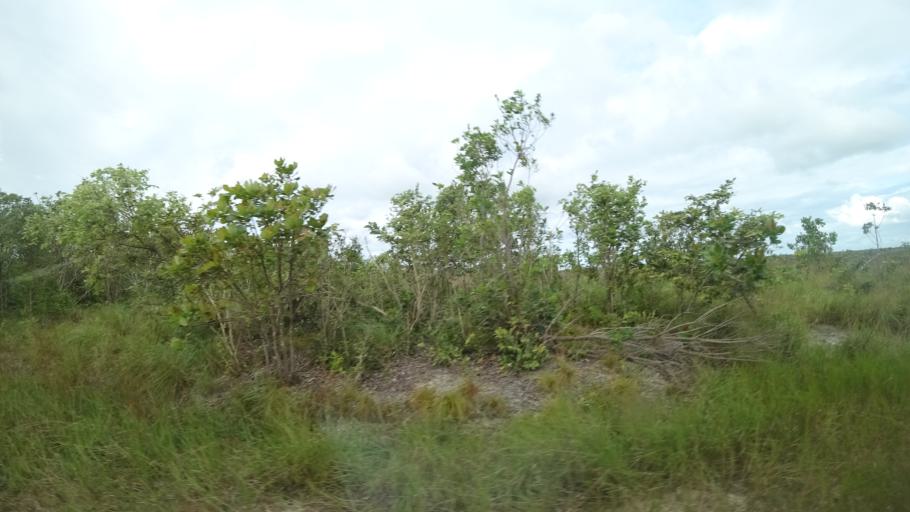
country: MZ
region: Sofala
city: Beira
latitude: -19.6224
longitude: 35.0607
